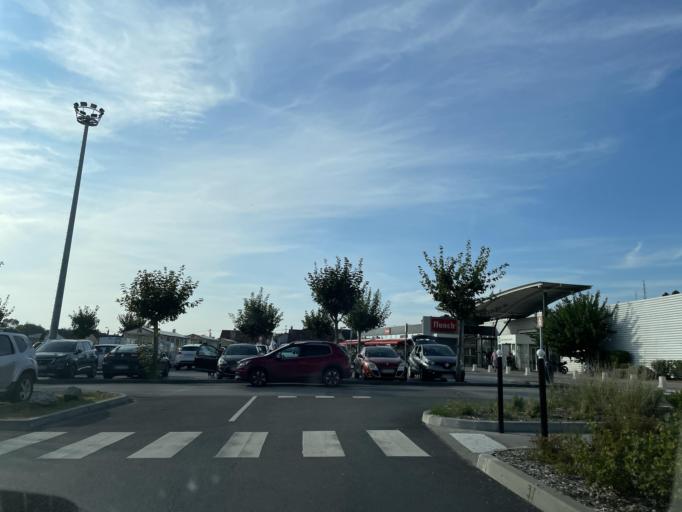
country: FR
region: Haute-Normandie
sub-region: Departement de la Seine-Maritime
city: Eu
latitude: 50.0618
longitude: 1.4081
